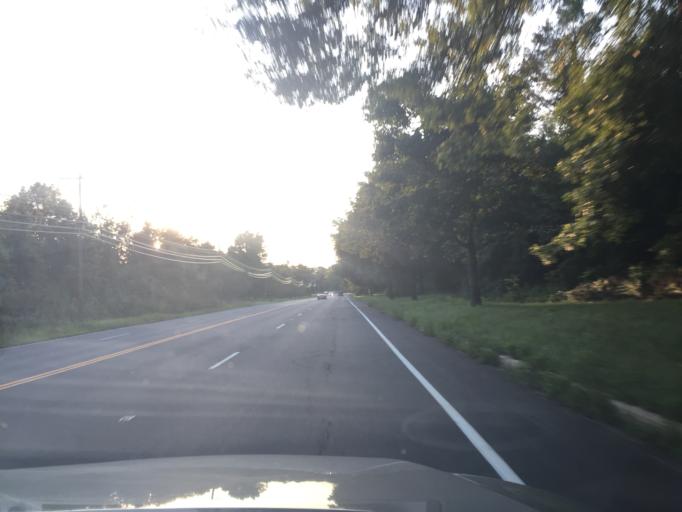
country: US
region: New Jersey
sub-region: Middlesex County
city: Plainsboro Center
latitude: 40.2924
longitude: -74.5878
